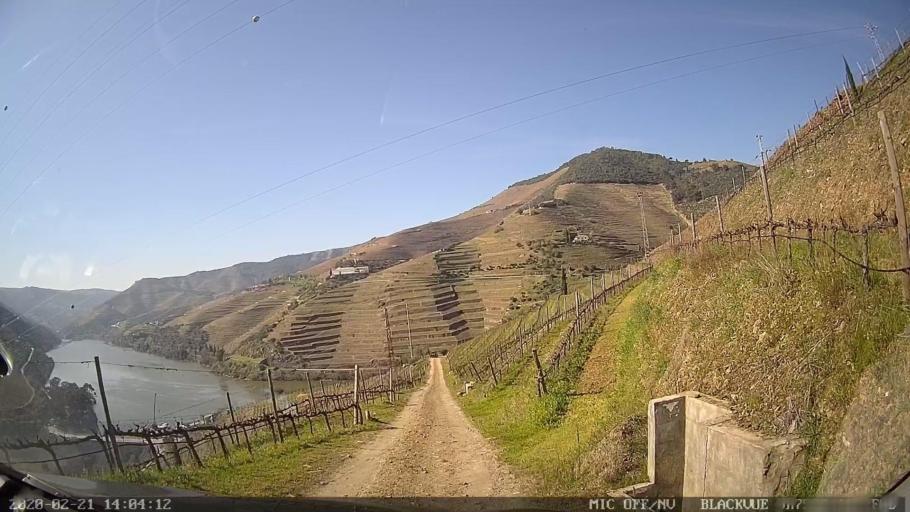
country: PT
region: Viseu
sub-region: Tabuaco
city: Tabuaco
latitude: 41.1756
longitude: -7.5498
